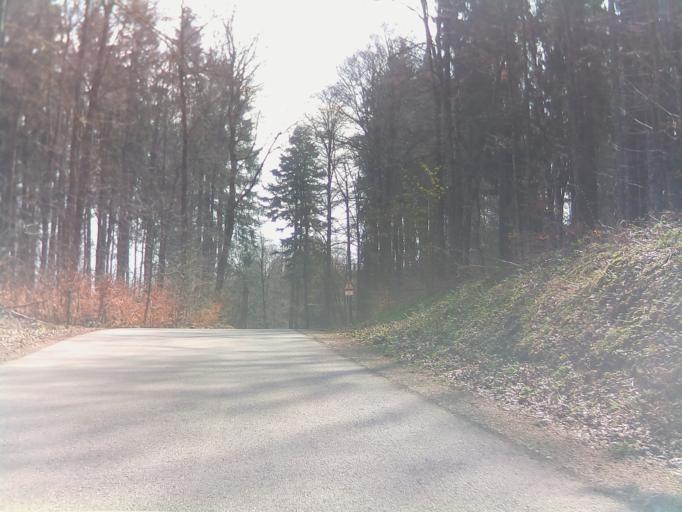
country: DE
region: Baden-Wuerttemberg
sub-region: Tuebingen Region
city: Gomadingen
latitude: 48.4372
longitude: 9.4226
